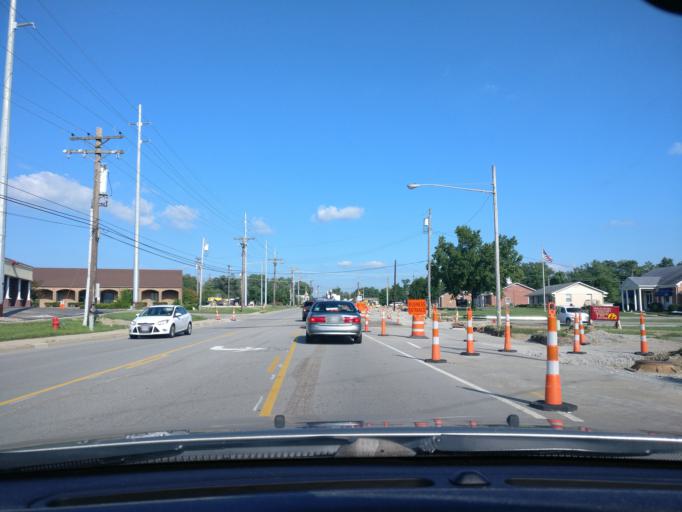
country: US
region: Ohio
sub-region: Warren County
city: Springboro
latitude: 39.5574
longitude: -84.2354
